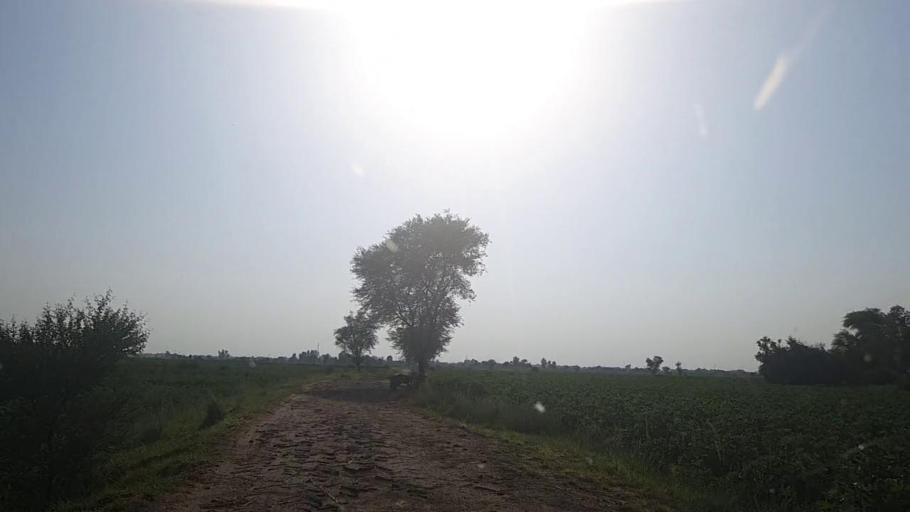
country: PK
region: Sindh
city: Khanpur
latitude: 27.7306
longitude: 69.3218
